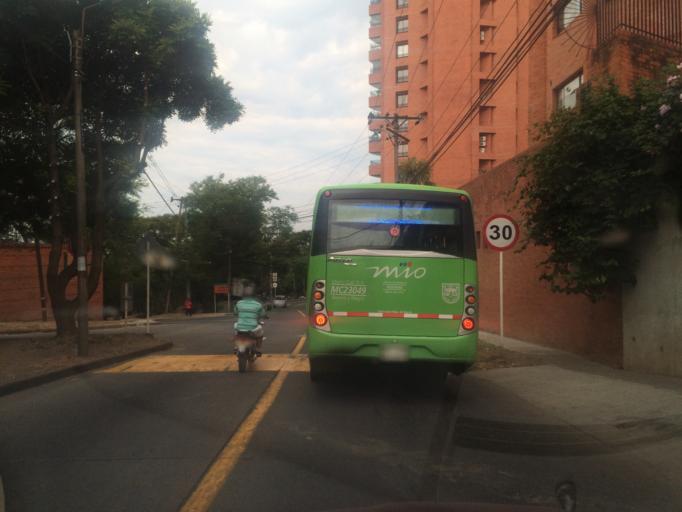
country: CO
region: Valle del Cauca
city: Cali
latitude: 3.4469
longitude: -76.5476
